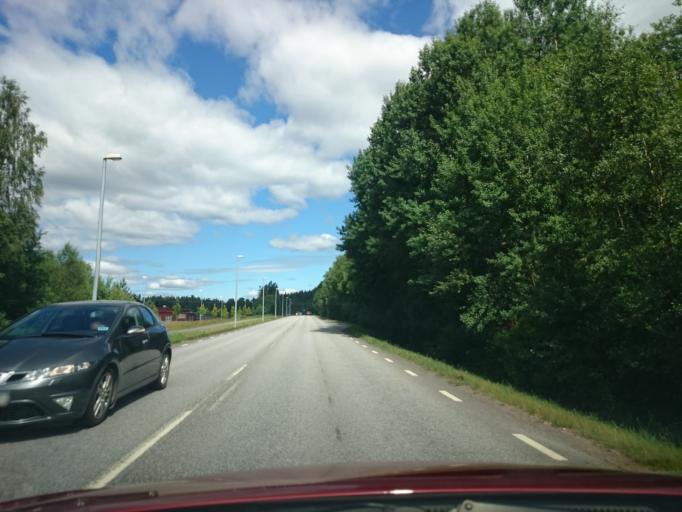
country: SE
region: Vaestra Goetaland
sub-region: Lerums Kommun
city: Stenkullen
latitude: 57.7996
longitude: 12.3077
